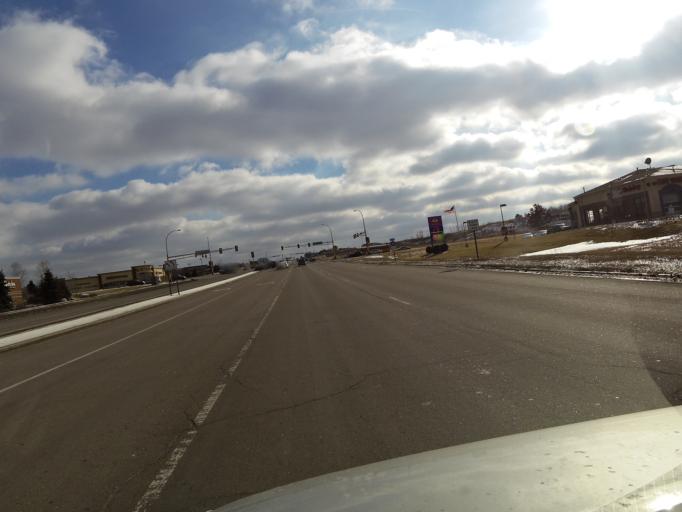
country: US
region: Minnesota
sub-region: Scott County
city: Shakopee
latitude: 44.7803
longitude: -93.4699
